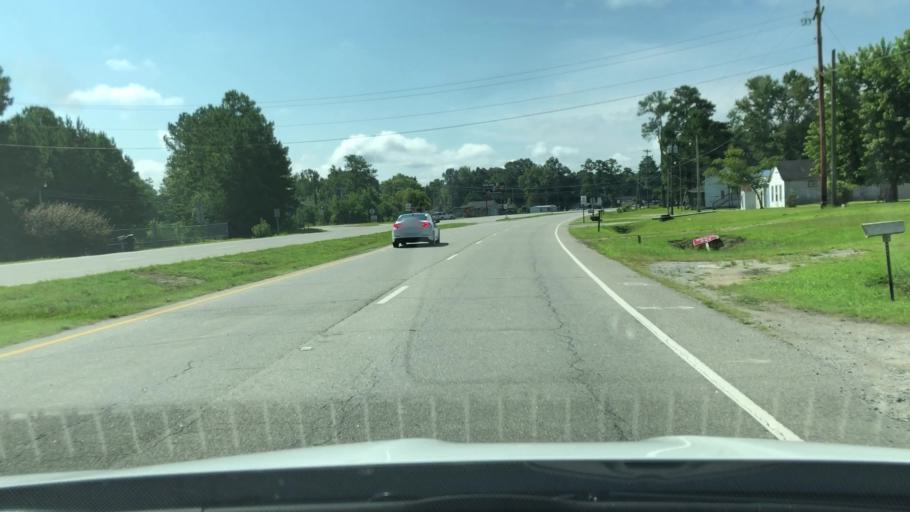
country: US
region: North Carolina
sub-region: Bertie County
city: Windsor
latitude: 35.9660
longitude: -76.9526
